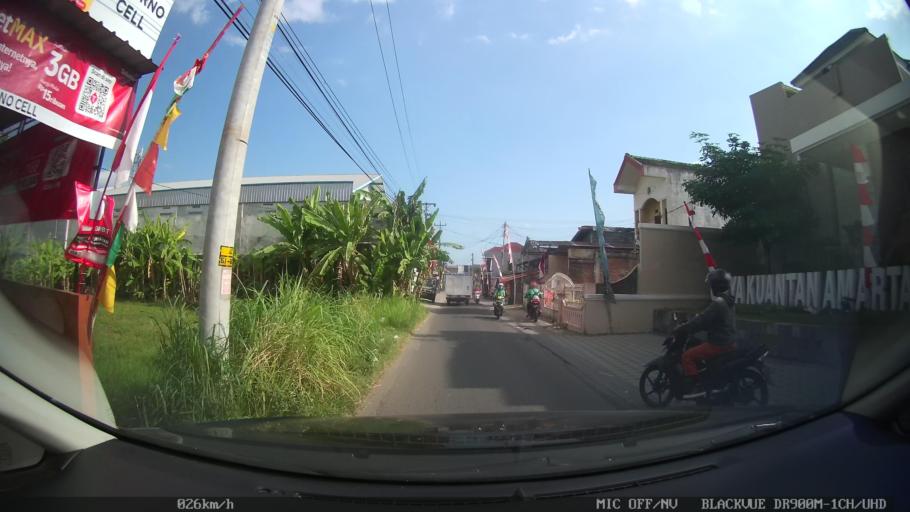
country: ID
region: Daerah Istimewa Yogyakarta
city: Gamping Lor
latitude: -7.7984
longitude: 110.3413
